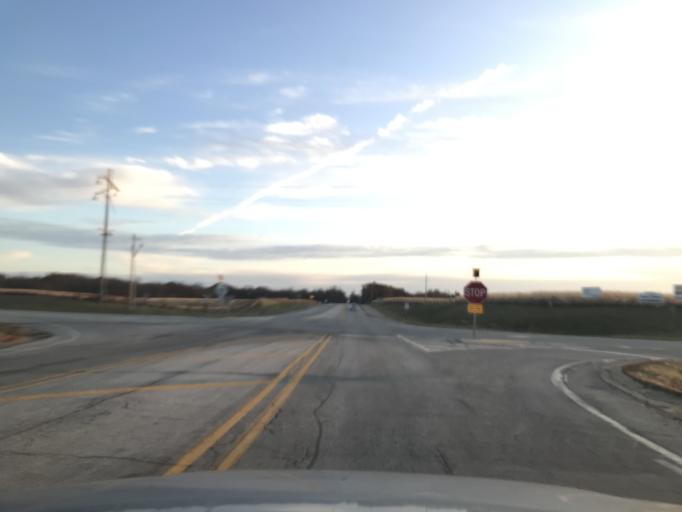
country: US
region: Illinois
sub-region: Henderson County
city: Oquawka
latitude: 40.9240
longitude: -90.8642
